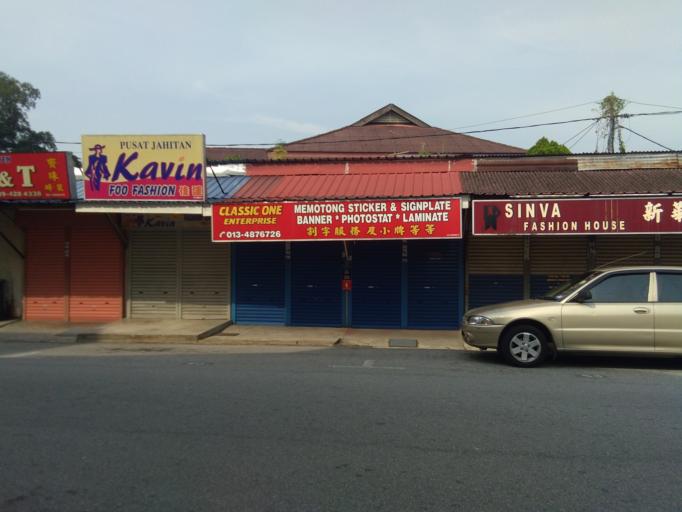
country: MY
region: Kedah
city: Kulim
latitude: 5.3701
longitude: 100.5542
